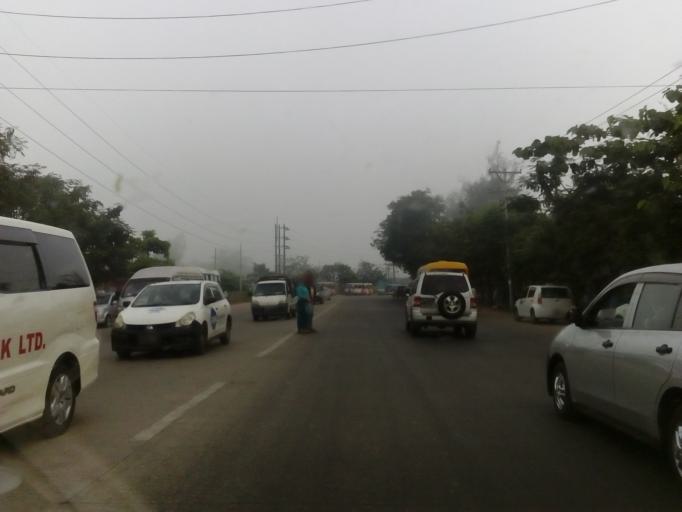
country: MM
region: Yangon
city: Yangon
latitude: 16.8096
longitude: 96.1836
